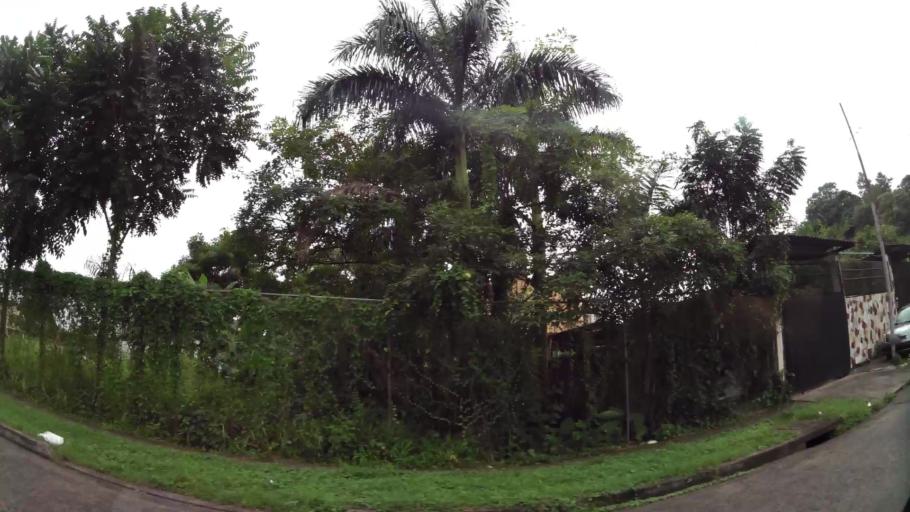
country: PA
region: Panama
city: Panama
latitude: 9.0219
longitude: -79.5186
